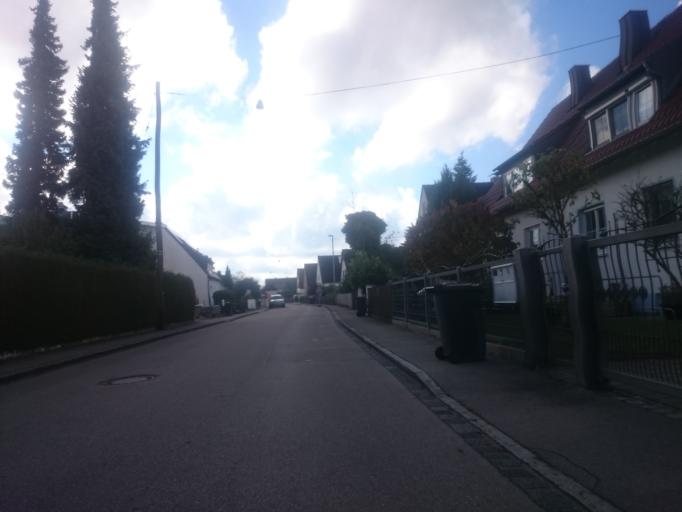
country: DE
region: Bavaria
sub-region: Swabia
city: Augsburg
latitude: 48.3776
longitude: 10.9428
